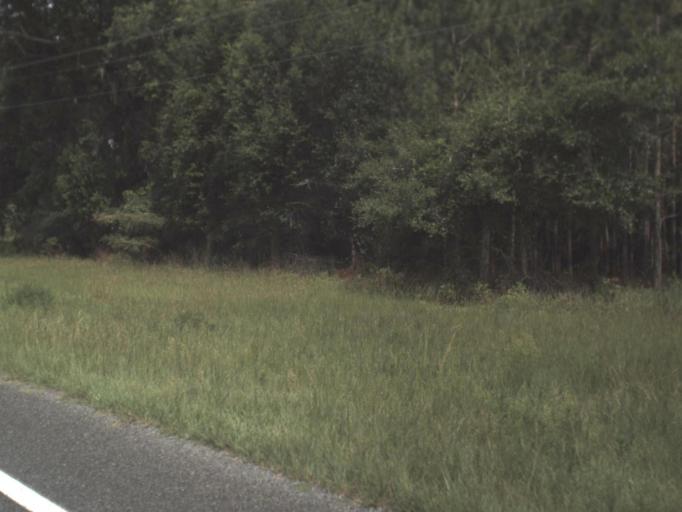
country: US
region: Florida
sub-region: Levy County
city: Chiefland
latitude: 29.4749
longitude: -82.8304
